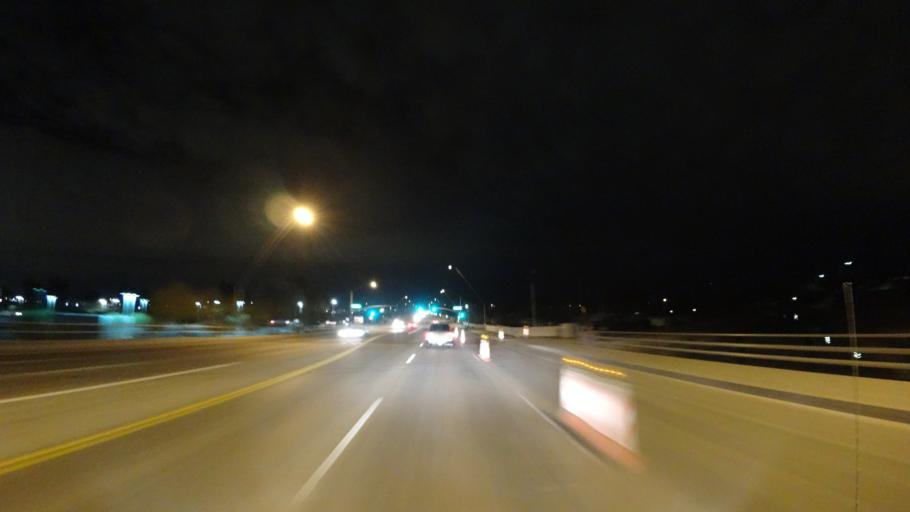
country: US
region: Arizona
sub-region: Maricopa County
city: Mesa
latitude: 33.4354
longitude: -111.8562
